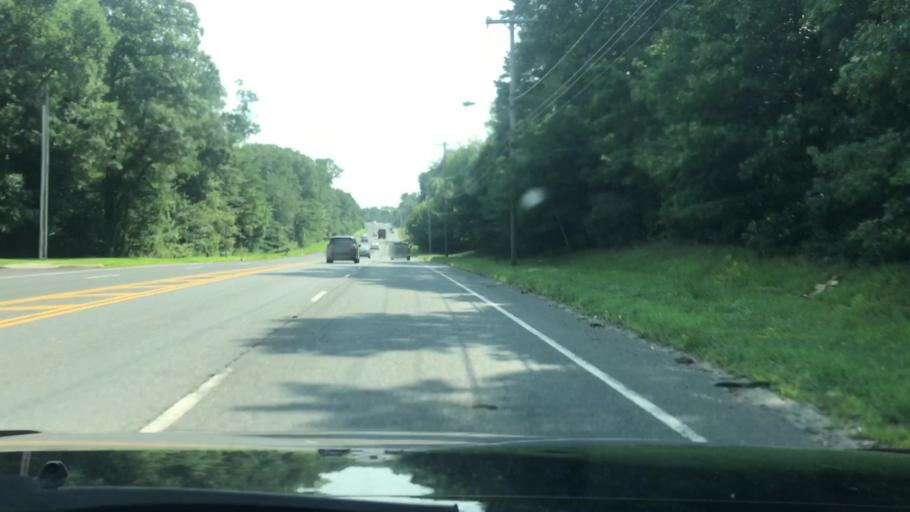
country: US
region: New Jersey
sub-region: Monmouth County
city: Farmingdale
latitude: 40.2297
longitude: -74.1141
